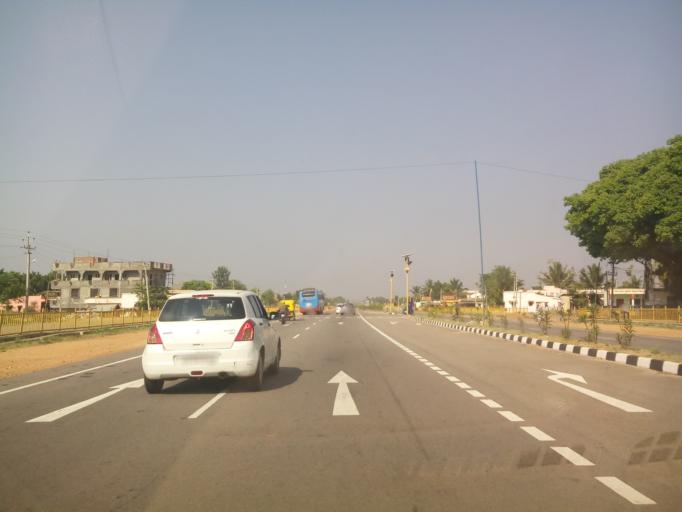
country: IN
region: Karnataka
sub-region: Tumkur
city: Kunigal
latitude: 12.9937
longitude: 76.8962
